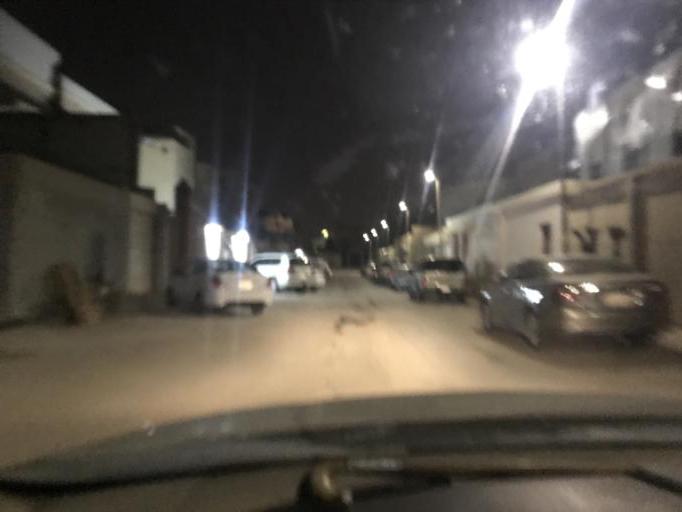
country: SA
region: Ar Riyad
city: Riyadh
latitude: 24.7419
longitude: 46.7657
